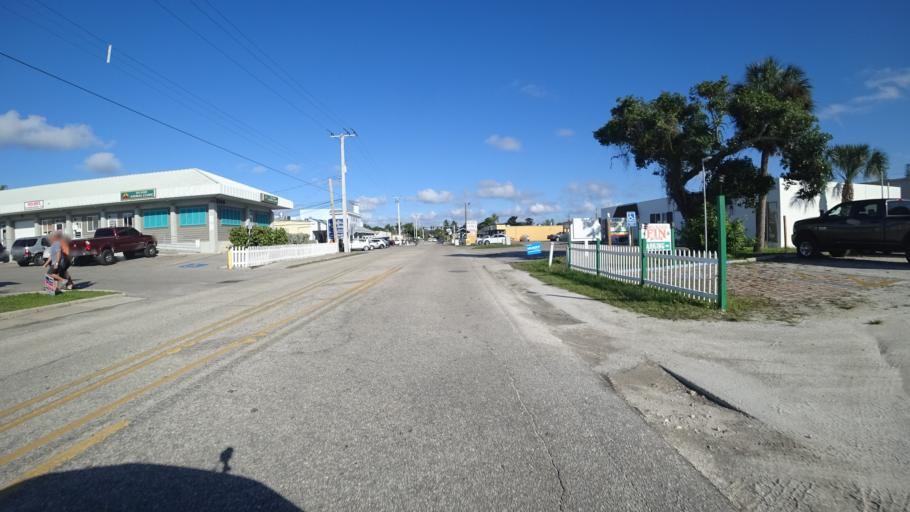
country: US
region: Florida
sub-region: Manatee County
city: Holmes Beach
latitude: 27.5058
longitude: -82.7160
